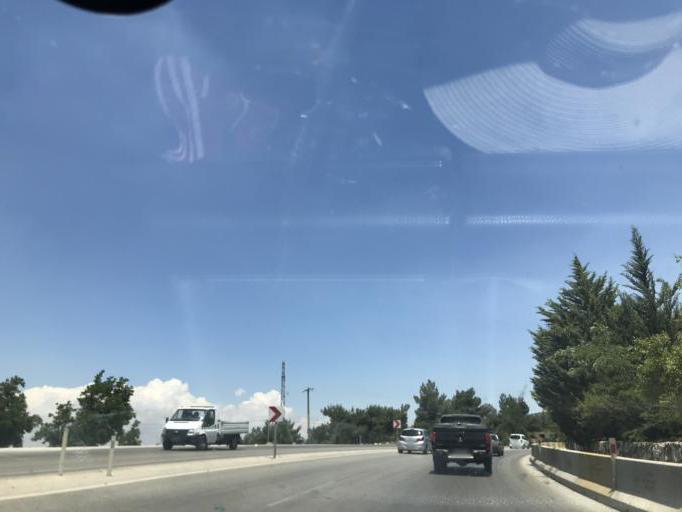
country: TR
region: Denizli
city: Honaz
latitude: 37.7322
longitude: 29.1782
